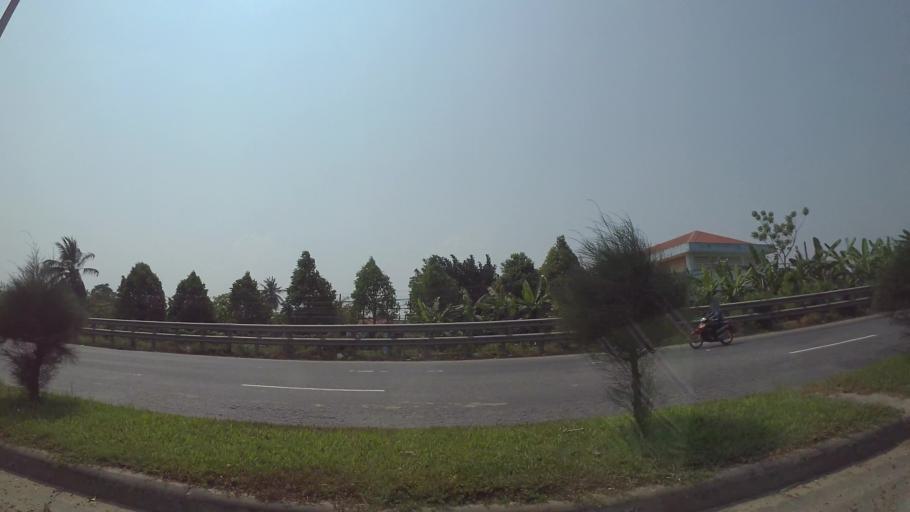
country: VN
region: Da Nang
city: Cam Le
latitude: 16.0028
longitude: 108.1903
